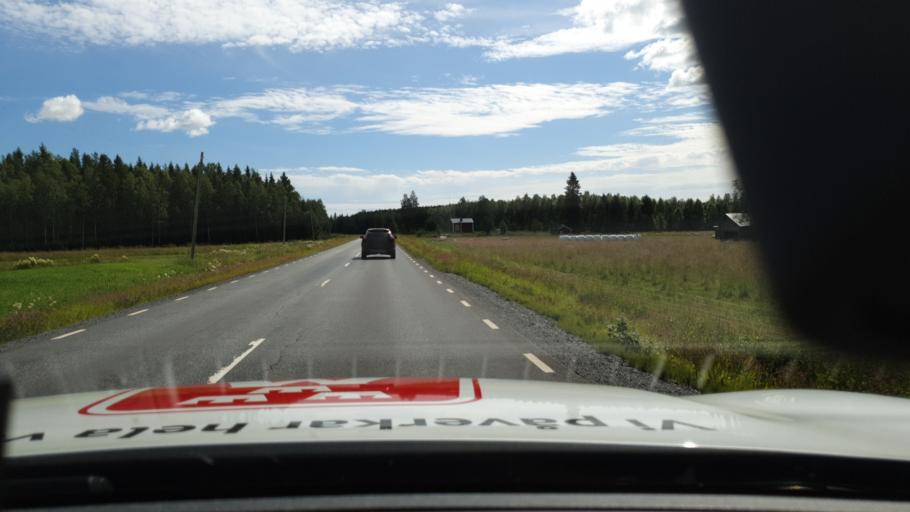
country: SE
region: Norrbotten
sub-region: Lulea Kommun
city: Ranea
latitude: 65.7864
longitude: 22.1582
